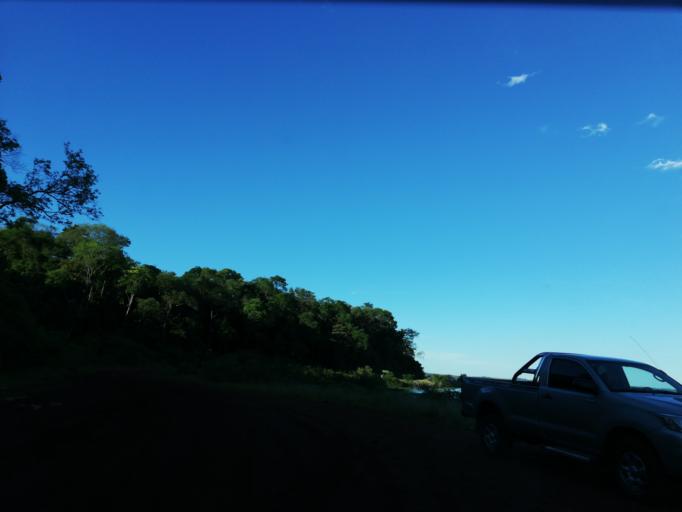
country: AR
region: Misiones
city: Garupa
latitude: -27.4616
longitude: -55.8157
